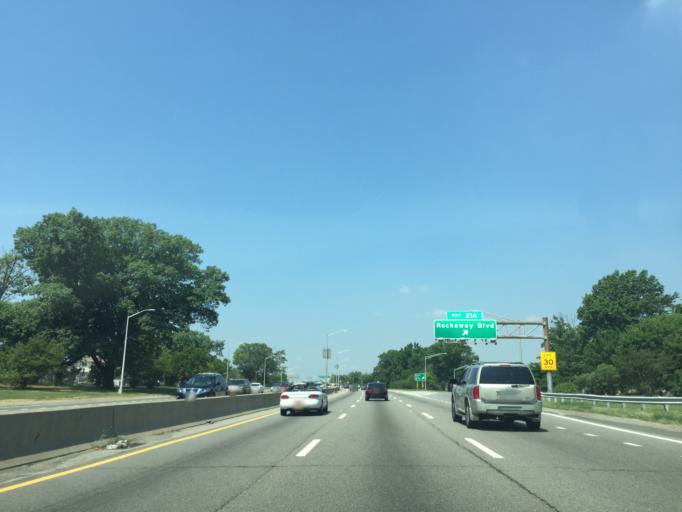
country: US
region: New York
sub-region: Queens County
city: Jamaica
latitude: 40.6676
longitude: -73.7717
